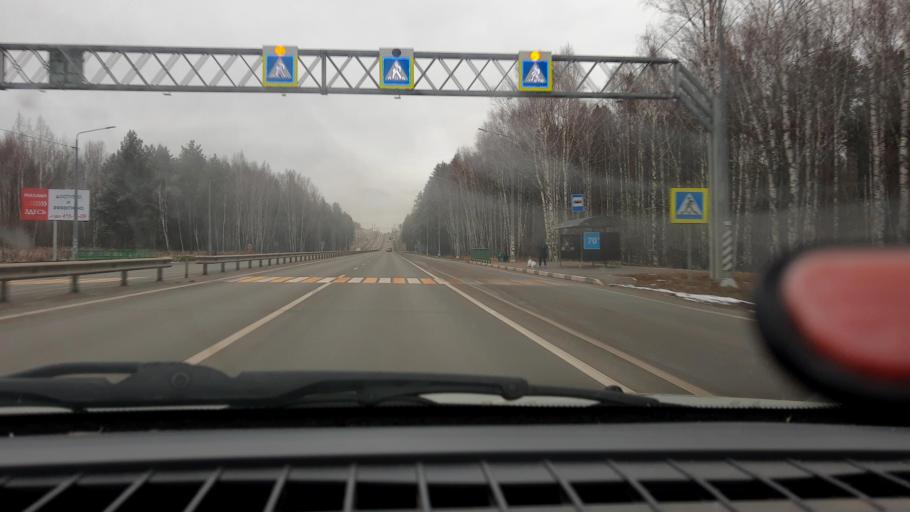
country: RU
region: Nizjnij Novgorod
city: Burevestnik
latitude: 56.0871
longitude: 43.9206
